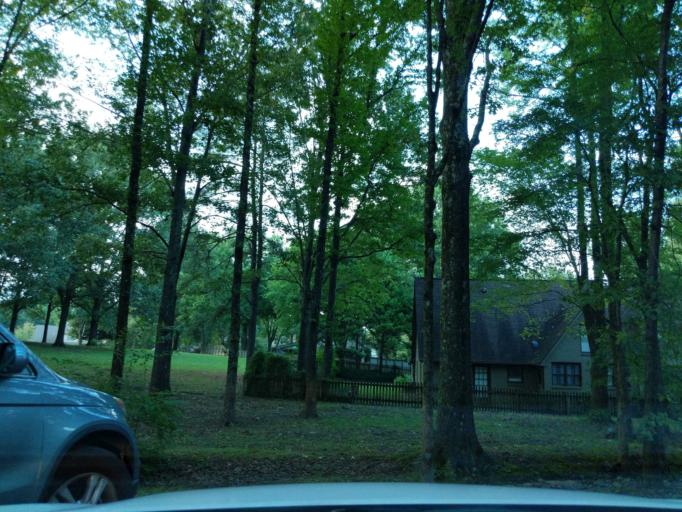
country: US
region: Tennessee
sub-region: Shelby County
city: Germantown
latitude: 35.0646
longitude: -89.7851
